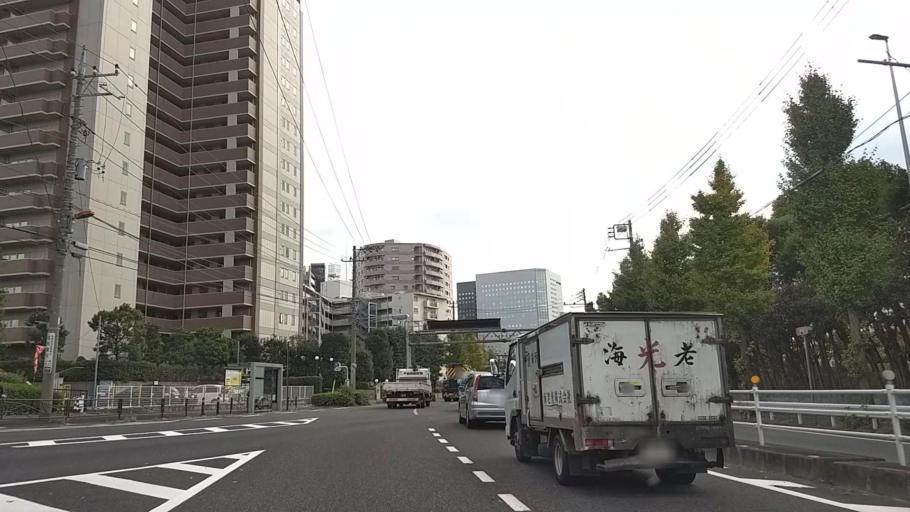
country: JP
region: Kanagawa
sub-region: Kawasaki-shi
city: Kawasaki
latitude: 35.5401
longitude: 139.6970
